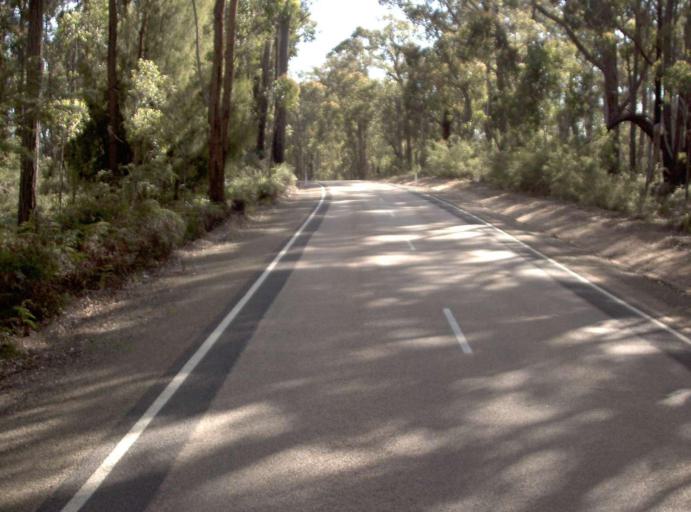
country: AU
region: Victoria
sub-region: East Gippsland
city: Lakes Entrance
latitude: -37.6880
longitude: 148.0469
